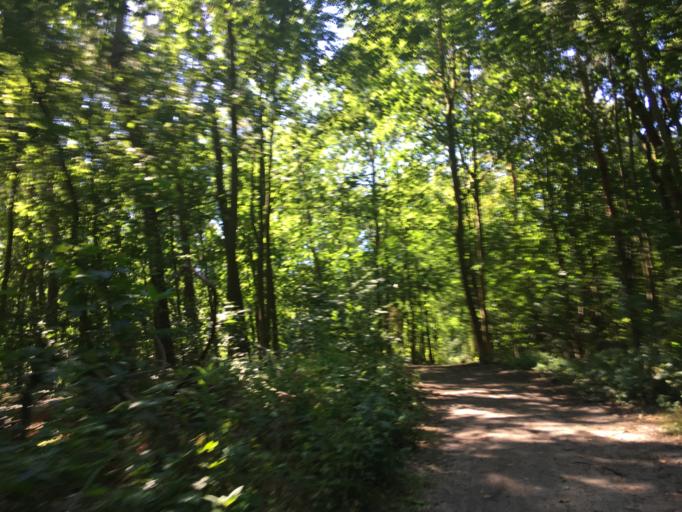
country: DE
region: Brandenburg
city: Erkner
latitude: 52.4268
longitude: 13.7638
